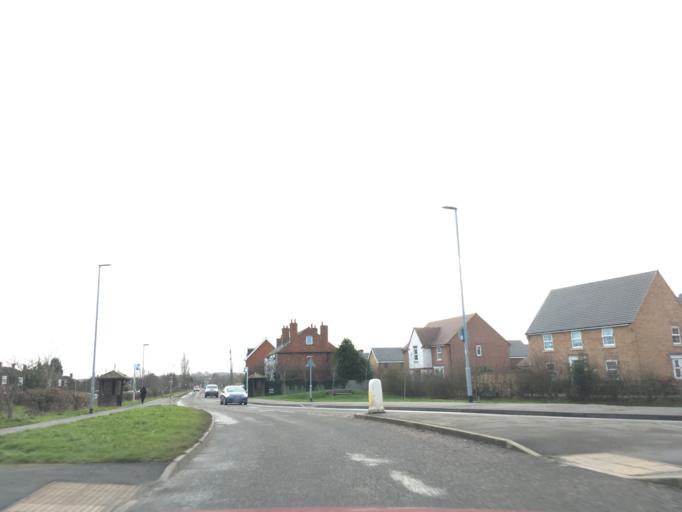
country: GB
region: England
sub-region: Nottinghamshire
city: East Leake
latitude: 52.8402
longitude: -1.1792
